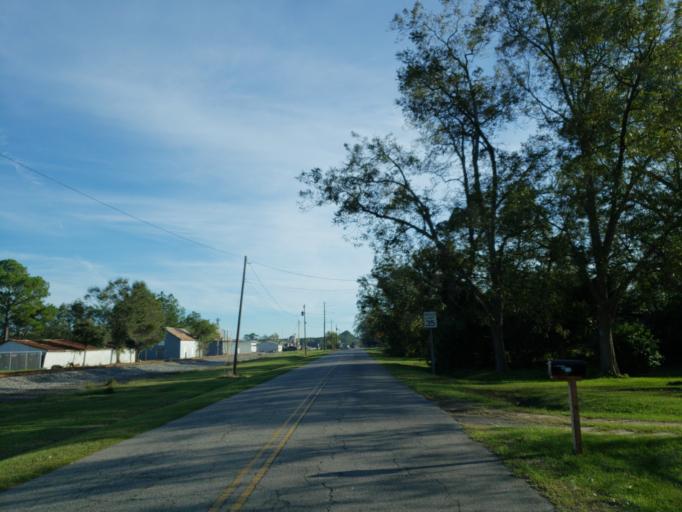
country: US
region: Georgia
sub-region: Dooly County
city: Vienna
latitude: 32.0965
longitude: -83.7877
